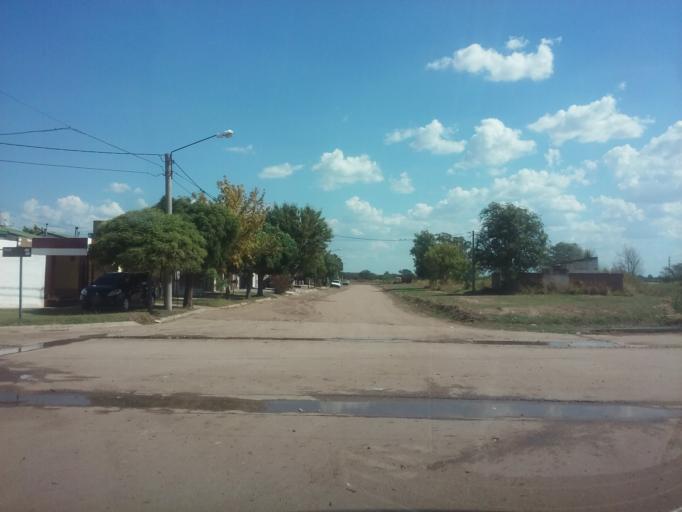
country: AR
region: La Pampa
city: Santa Rosa
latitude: -36.6456
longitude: -64.2967
